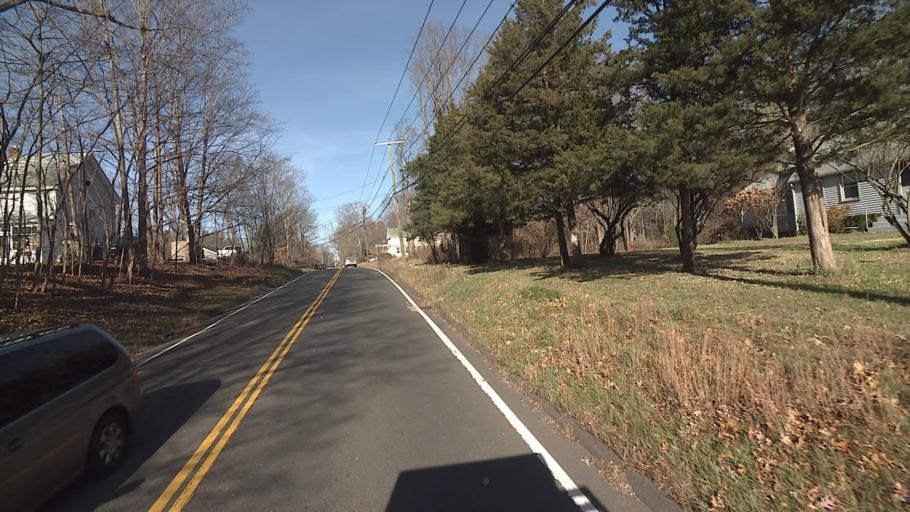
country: US
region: Connecticut
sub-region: Middlesex County
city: Cromwell
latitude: 41.6338
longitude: -72.6045
